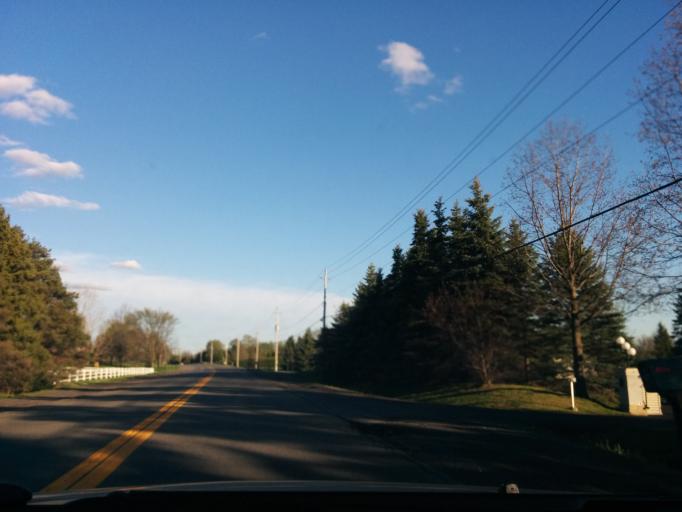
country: CA
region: Ontario
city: Bells Corners
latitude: 45.2159
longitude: -75.6594
